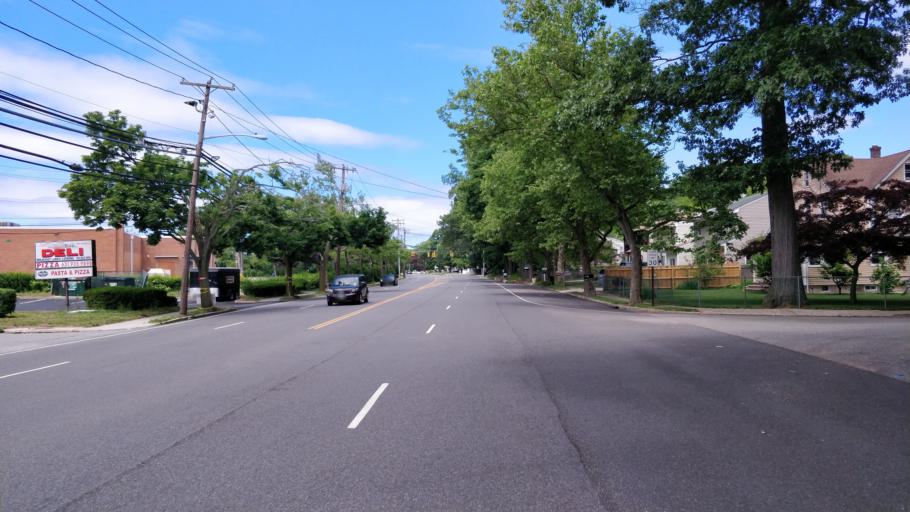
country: US
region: New York
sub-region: Suffolk County
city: South Huntington
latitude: 40.8168
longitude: -73.4077
